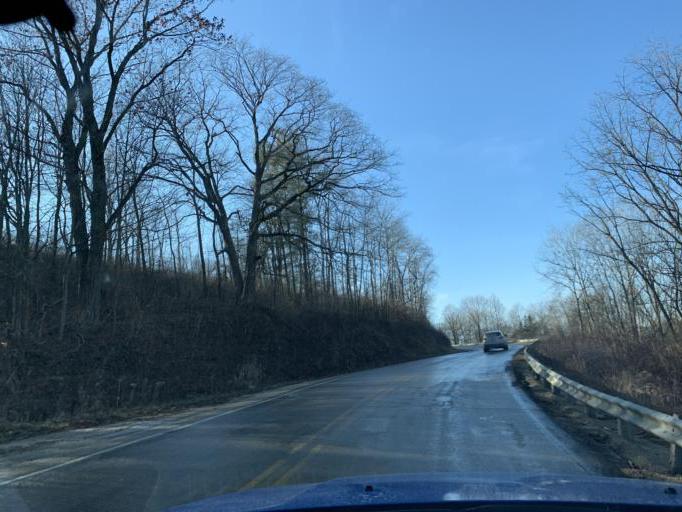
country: US
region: Wisconsin
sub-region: Iowa County
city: Barneveld
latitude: 42.8082
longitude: -89.8681
